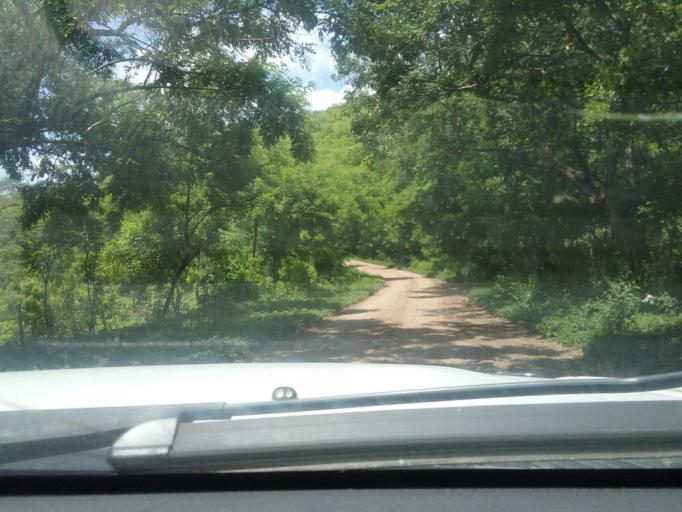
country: NI
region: Matagalpa
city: Terrabona
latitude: 12.6988
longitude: -85.9503
